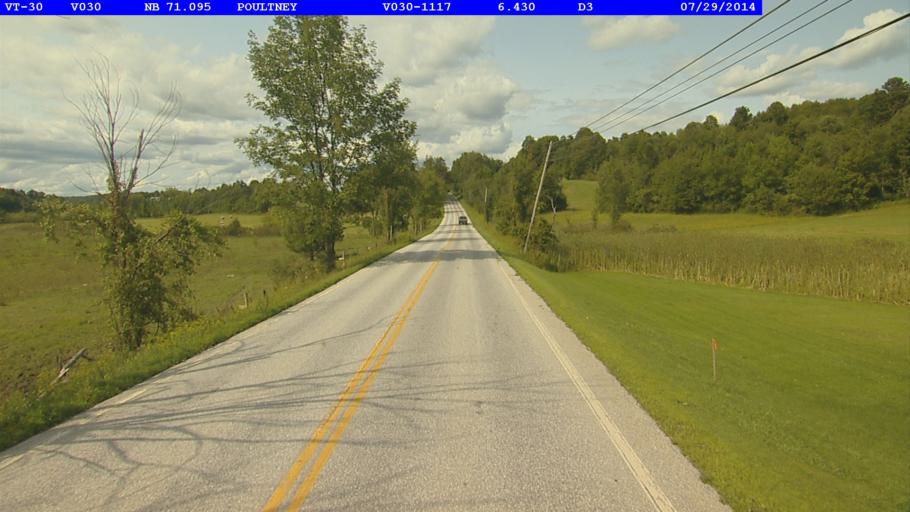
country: US
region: Vermont
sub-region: Rutland County
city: Poultney
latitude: 43.5436
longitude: -73.2275
